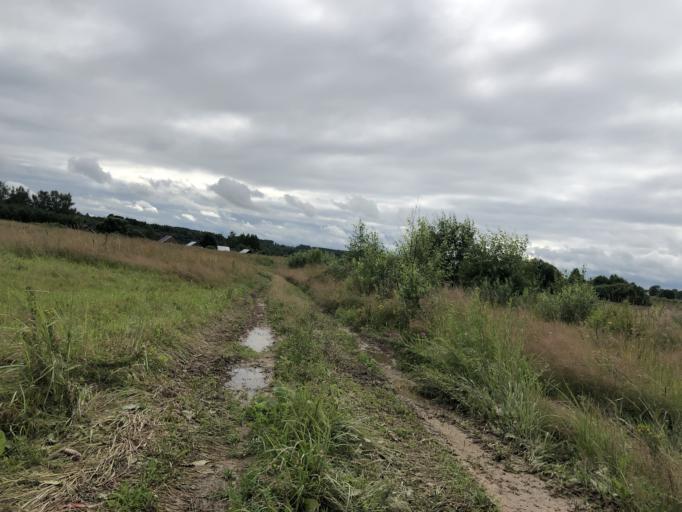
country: RU
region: Tverskaya
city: Rzhev
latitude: 56.2361
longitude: 34.3818
